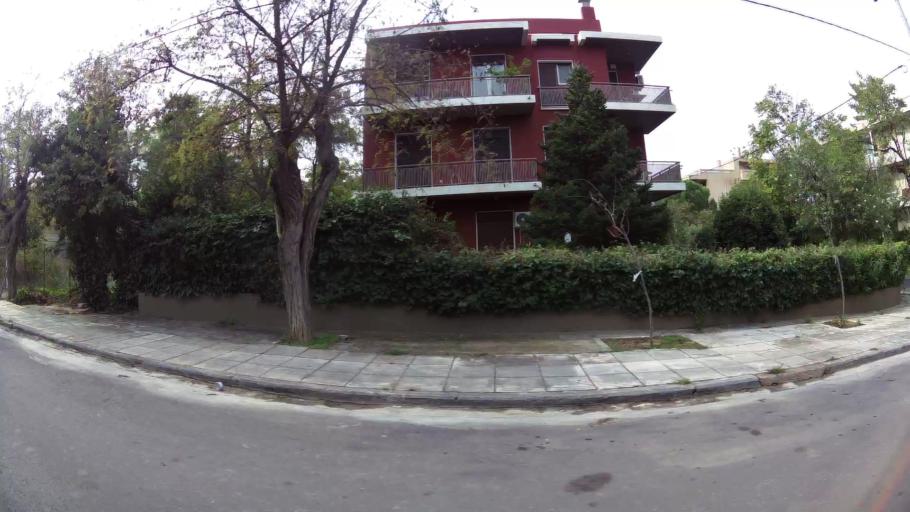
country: GR
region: Attica
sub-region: Nomarchia Athinas
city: Filothei
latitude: 38.0271
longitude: 23.7773
